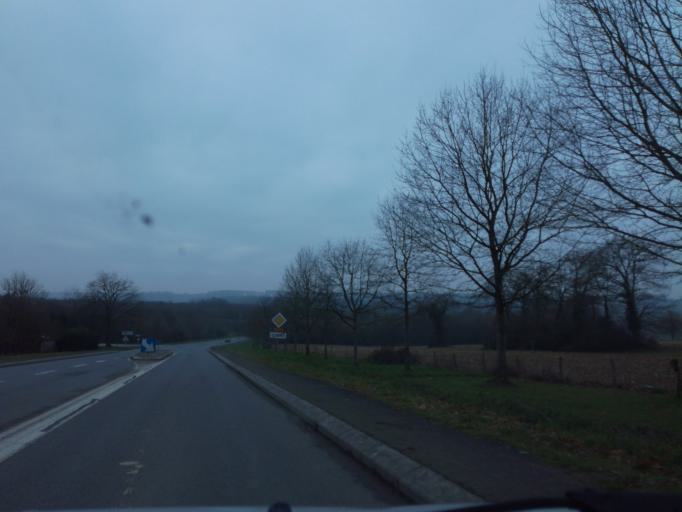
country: FR
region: Brittany
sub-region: Departement d'Ille-et-Vilaine
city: Gosne
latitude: 48.2441
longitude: -1.4610
